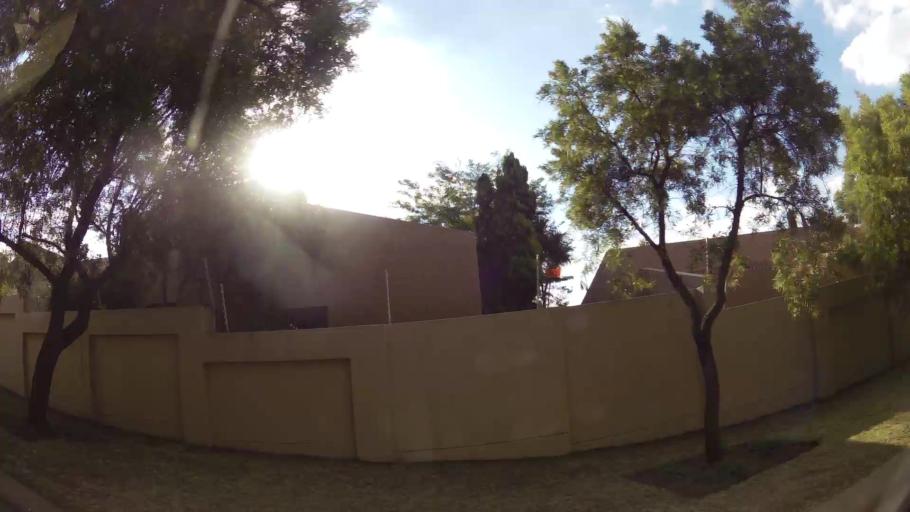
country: ZA
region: Gauteng
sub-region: City of Johannesburg Metropolitan Municipality
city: Diepsloot
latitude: -26.0062
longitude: 28.0294
